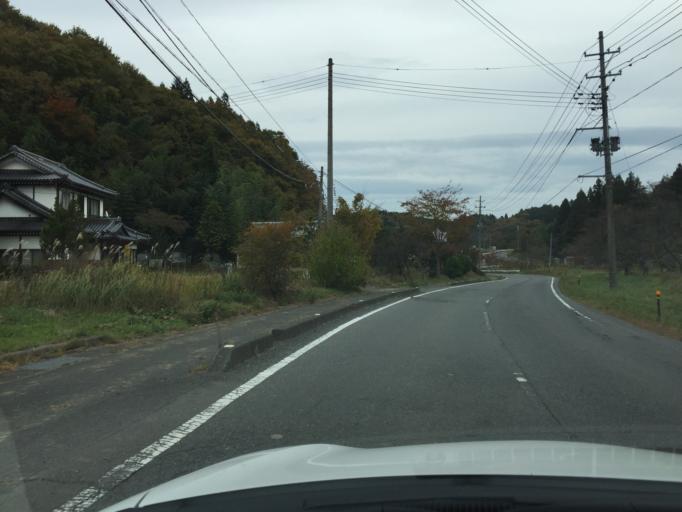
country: JP
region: Fukushima
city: Ishikawa
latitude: 37.1949
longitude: 140.6309
